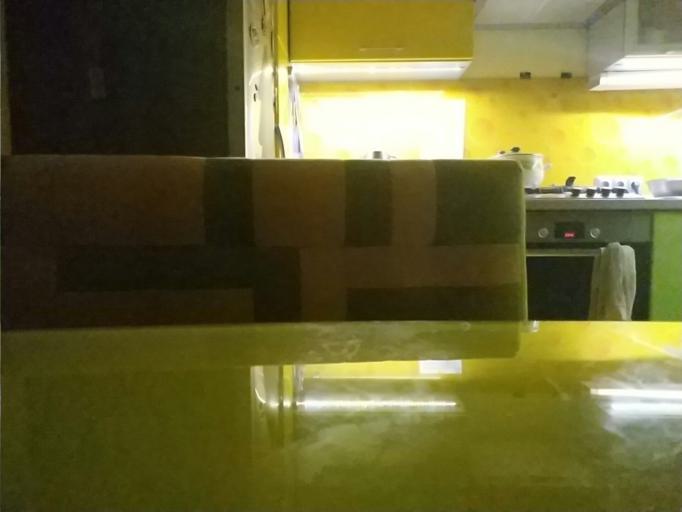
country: RU
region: Republic of Karelia
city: Pyaozerskiy
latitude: 65.7723
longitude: 30.4857
